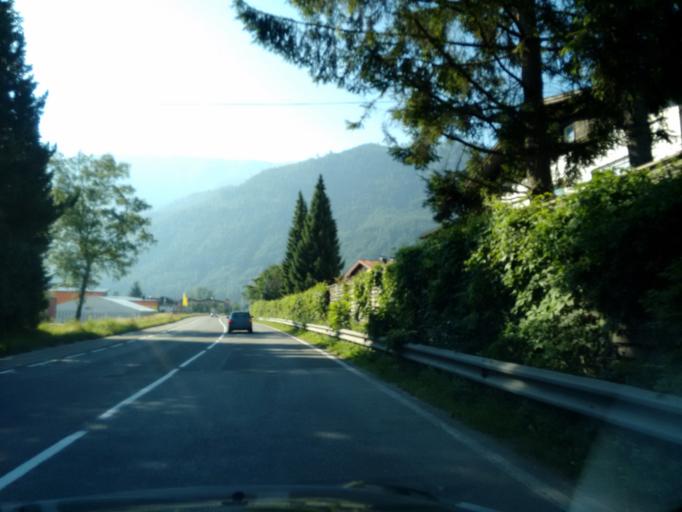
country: AT
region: Upper Austria
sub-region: Politischer Bezirk Gmunden
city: Ebensee
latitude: 47.8073
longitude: 13.7788
